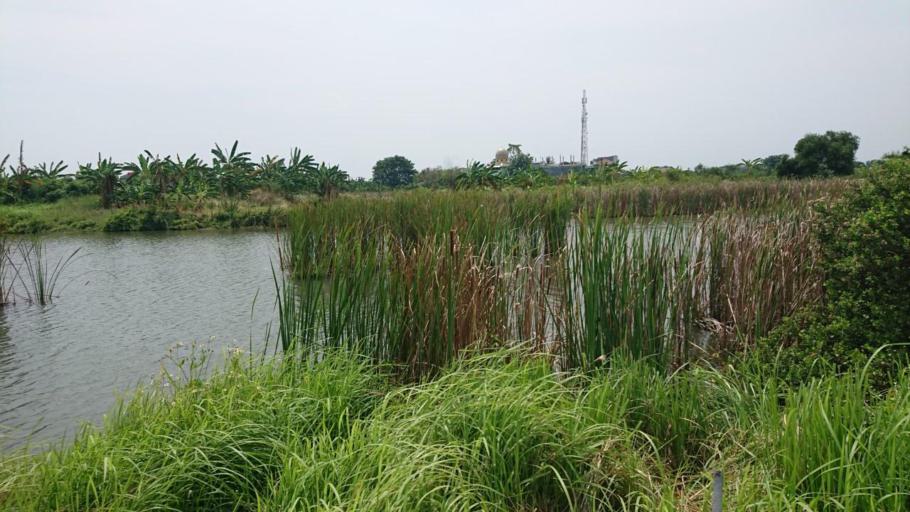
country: ID
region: West Java
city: Bekasi
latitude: -6.1297
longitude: 106.9627
